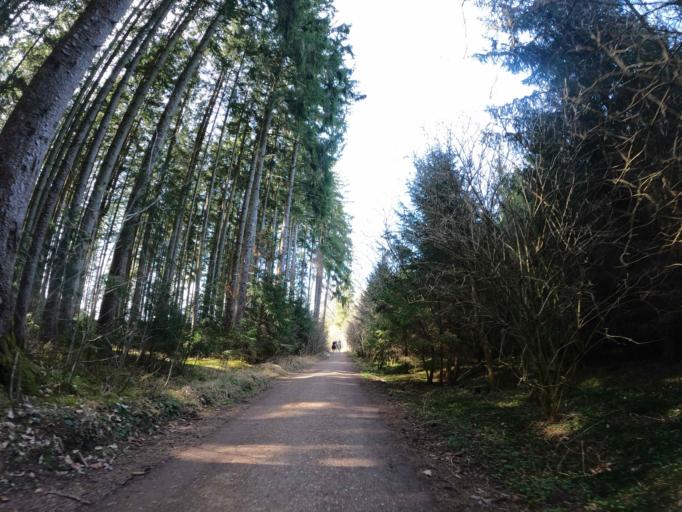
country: DE
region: Bavaria
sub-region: Upper Bavaria
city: Brunnthal
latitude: 47.9994
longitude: 11.6973
